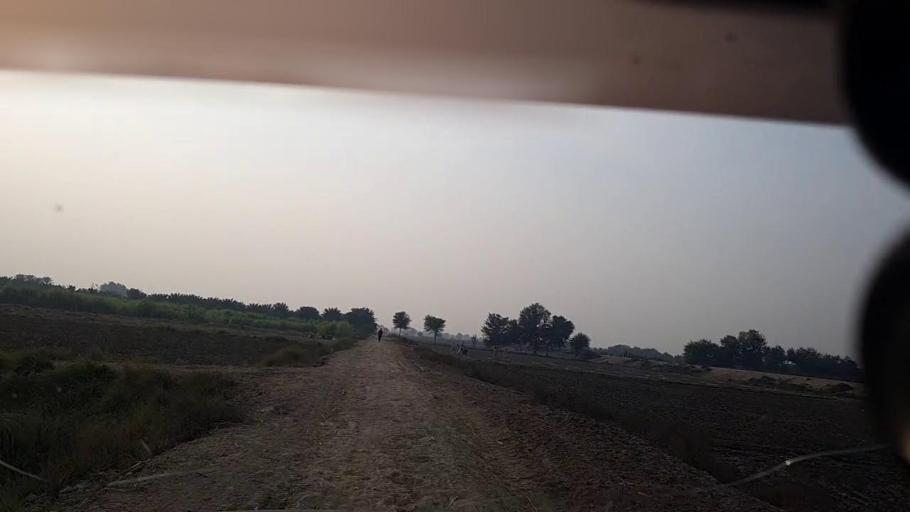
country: PK
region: Sindh
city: Gambat
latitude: 27.4355
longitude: 68.6014
